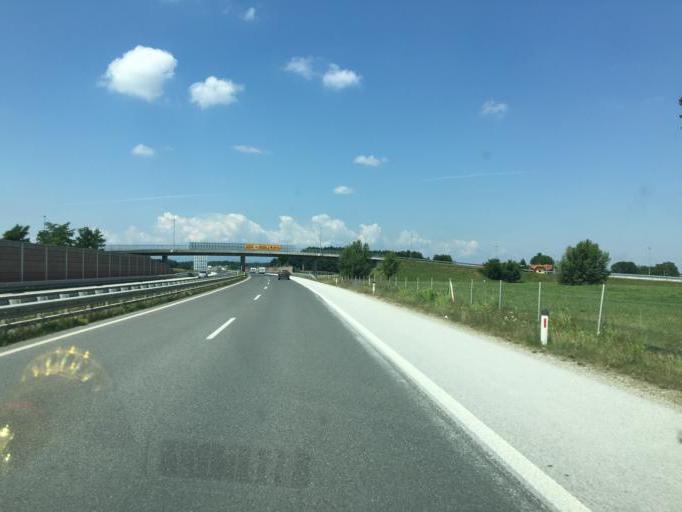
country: SI
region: Hajdina
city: Spodnja Hajdina
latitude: 46.3978
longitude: 15.8454
